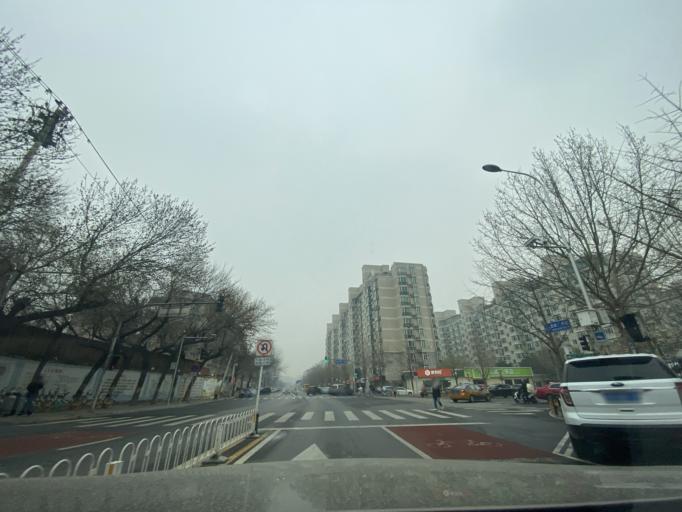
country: CN
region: Beijing
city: Sijiqing
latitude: 39.9650
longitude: 116.2734
